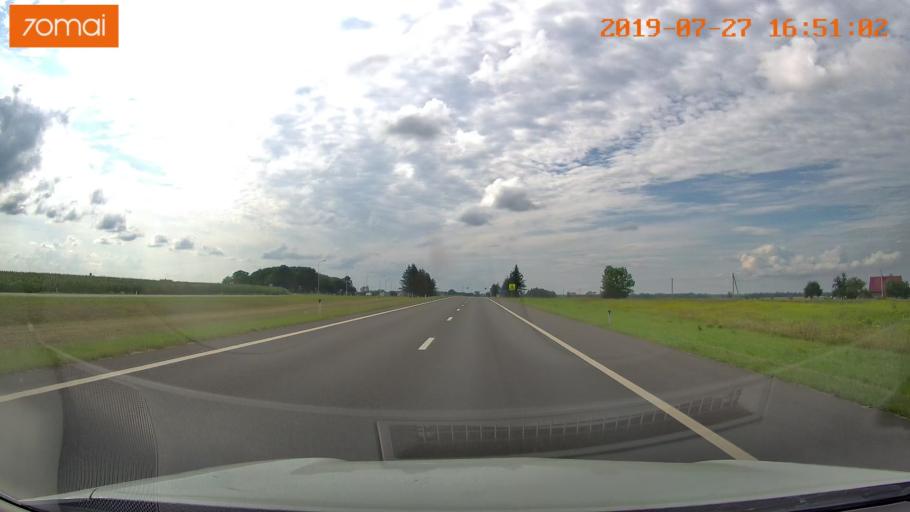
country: RU
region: Kaliningrad
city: Gvardeysk
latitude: 54.6806
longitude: 20.8979
